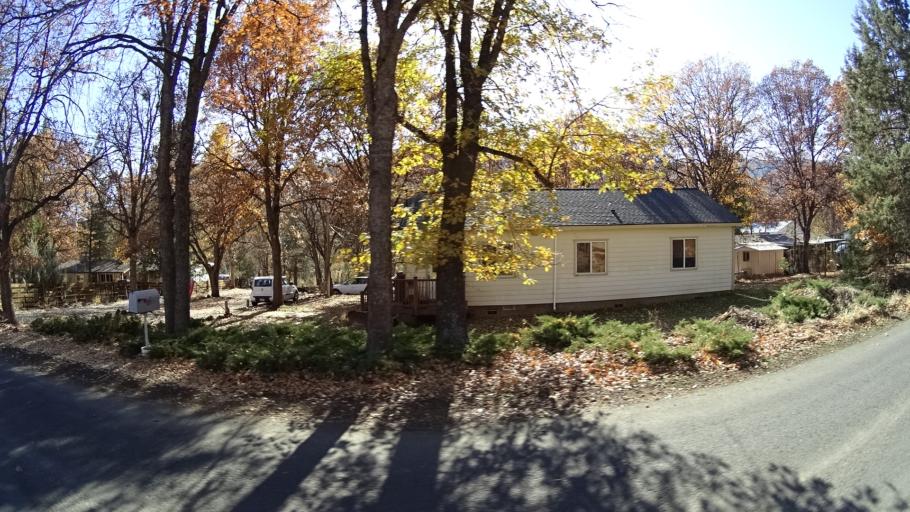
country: US
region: California
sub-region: Siskiyou County
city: Yreka
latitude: 41.7148
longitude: -122.6581
